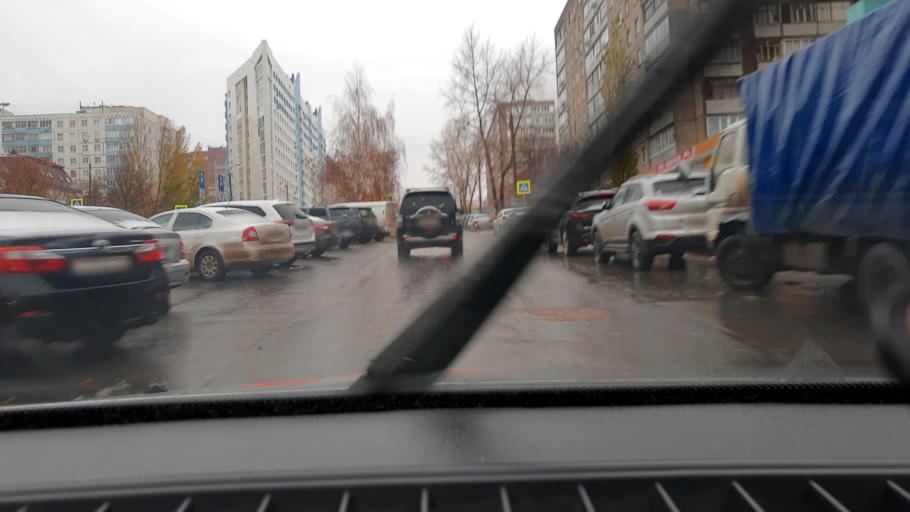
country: RU
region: Bashkortostan
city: Ufa
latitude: 54.7337
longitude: 55.9958
